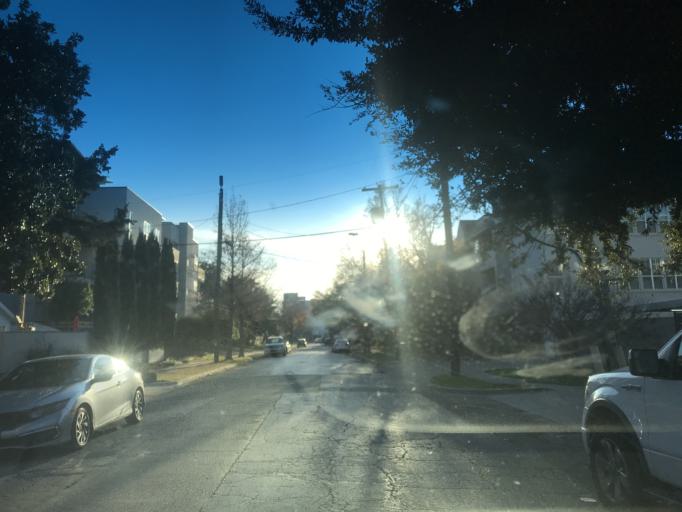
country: US
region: Texas
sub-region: Dallas County
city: Highland Park
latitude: 32.8136
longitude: -96.8105
